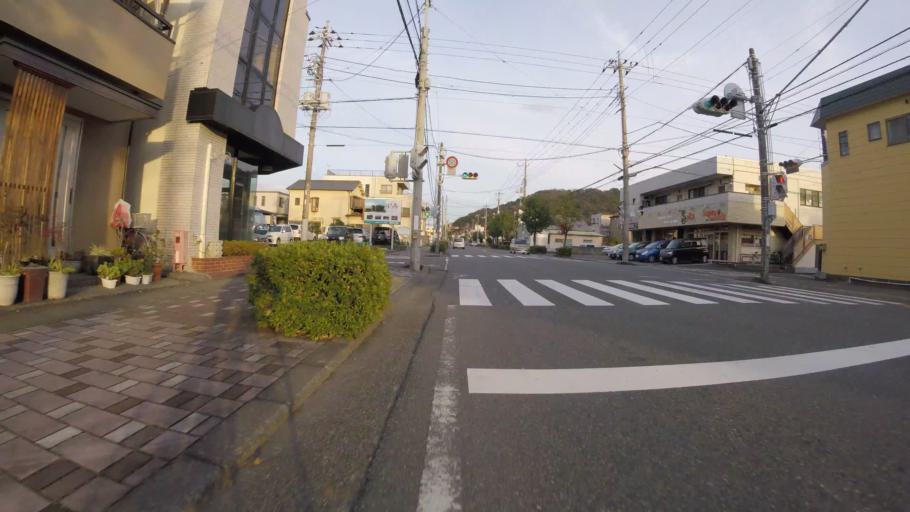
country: JP
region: Shizuoka
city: Numazu
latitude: 35.0966
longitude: 138.8657
